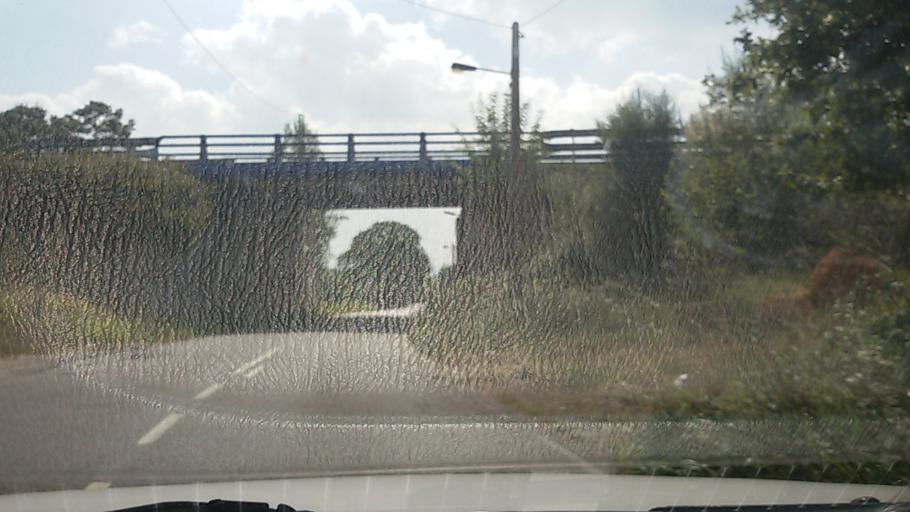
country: ES
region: Asturias
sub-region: Province of Asturias
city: Lugones
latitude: 43.4386
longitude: -5.8062
